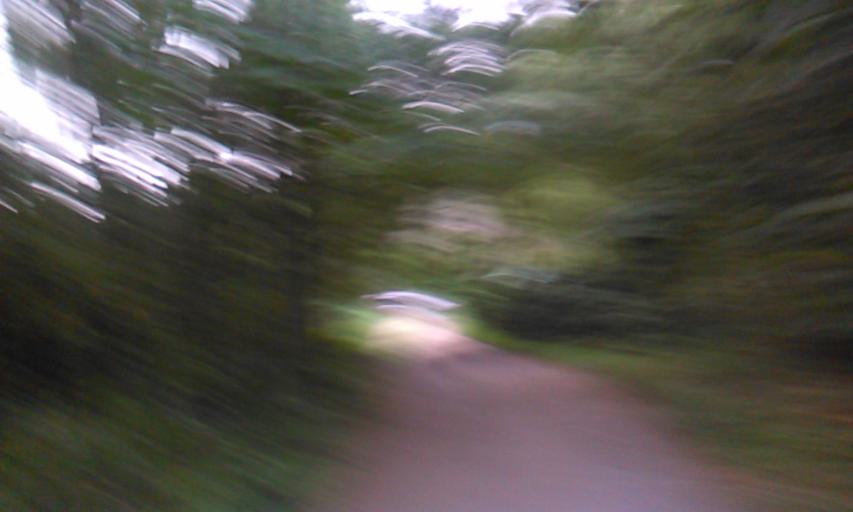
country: CO
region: Quindio
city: Cordoba
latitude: 4.4034
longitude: -75.6878
